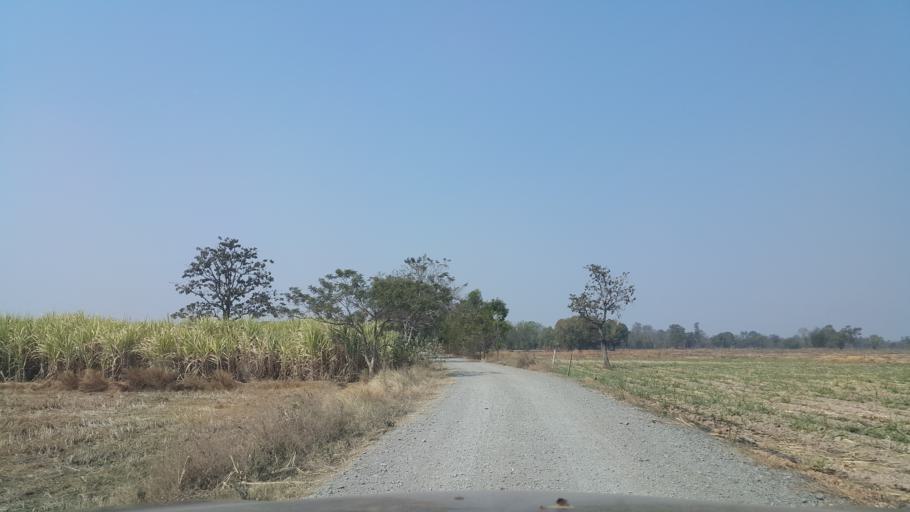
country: TH
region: Buriram
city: Krasang
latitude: 15.0909
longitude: 103.3794
